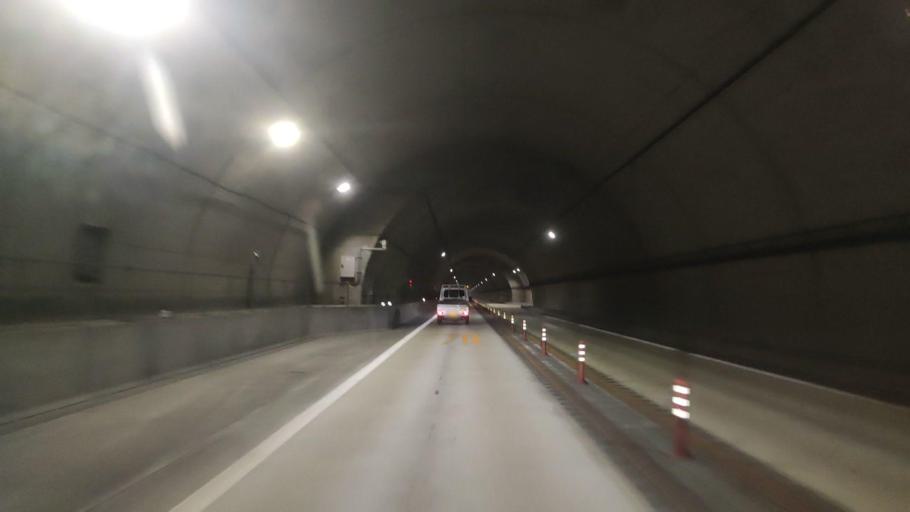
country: JP
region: Wakayama
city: Tanabe
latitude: 33.6220
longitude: 135.4193
